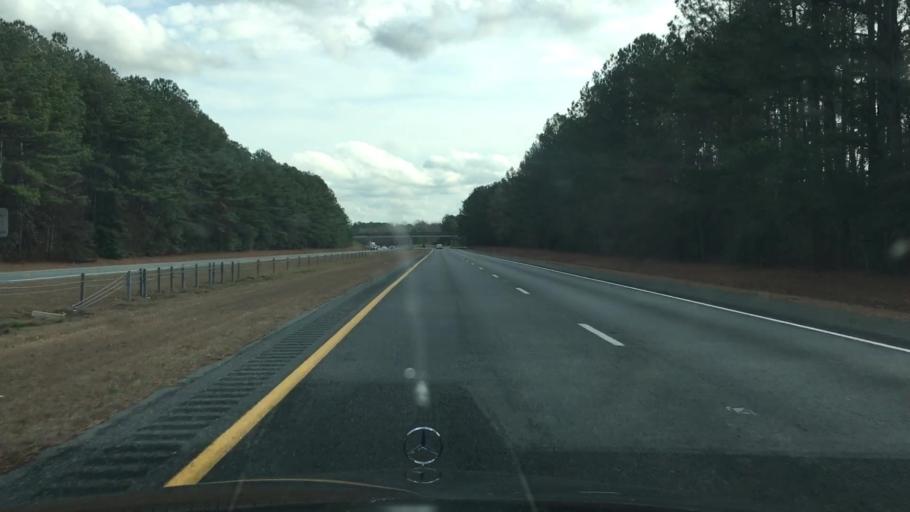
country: US
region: North Carolina
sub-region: Sampson County
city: Clinton
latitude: 35.2168
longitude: -78.3319
